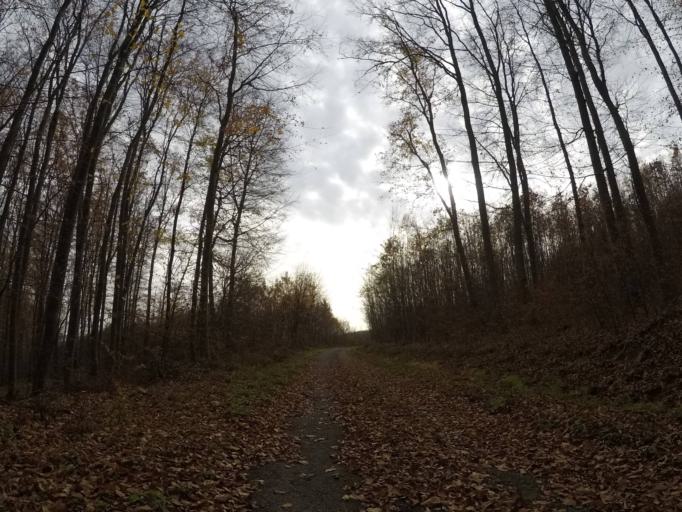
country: SK
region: Presovsky
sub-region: Okres Presov
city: Presov
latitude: 48.9667
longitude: 21.1837
